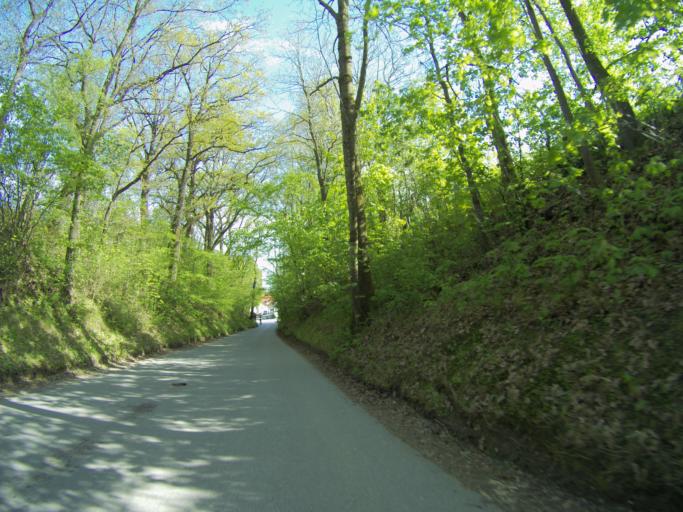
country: DE
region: Bavaria
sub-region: Upper Bavaria
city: Freising
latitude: 48.3991
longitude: 11.7163
